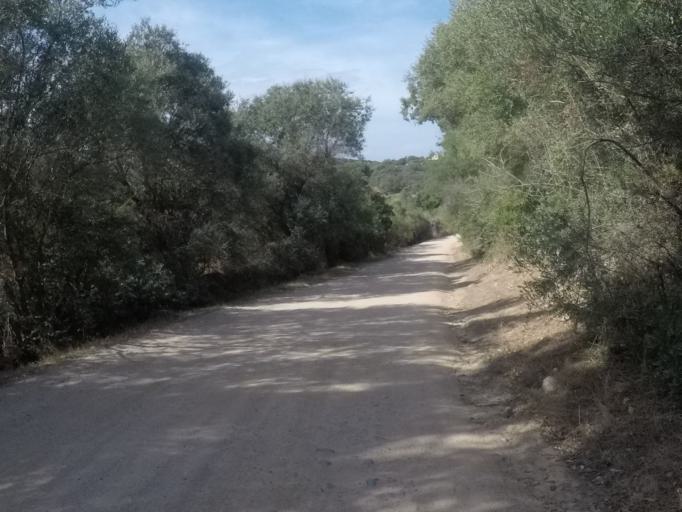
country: IT
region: Sardinia
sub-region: Provincia di Olbia-Tempio
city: Arzachena
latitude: 41.0476
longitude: 9.3612
